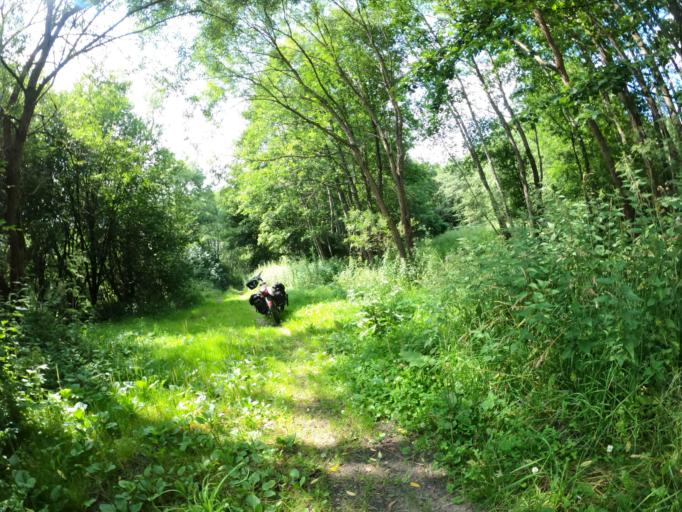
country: PL
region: West Pomeranian Voivodeship
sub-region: Powiat szczecinecki
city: Grzmiaca
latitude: 53.8309
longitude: 16.4497
